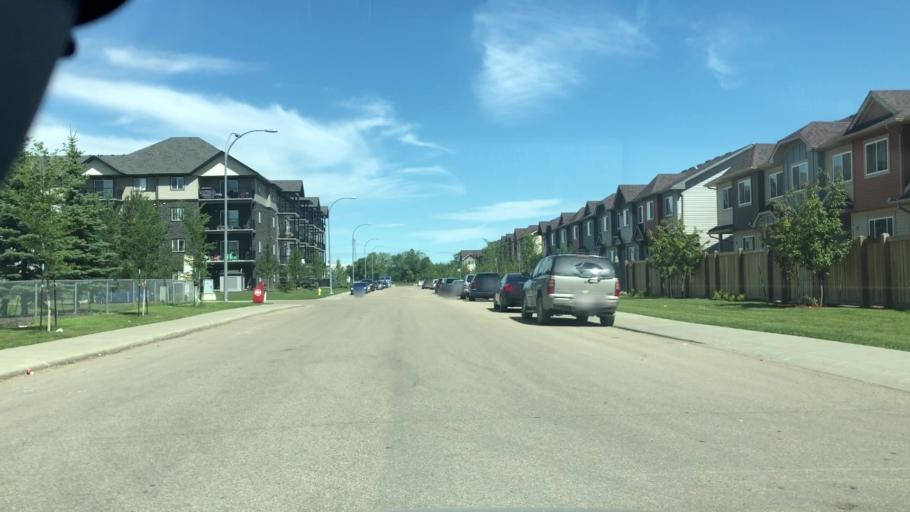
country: CA
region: Alberta
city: Edmonton
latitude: 53.6099
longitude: -113.5378
